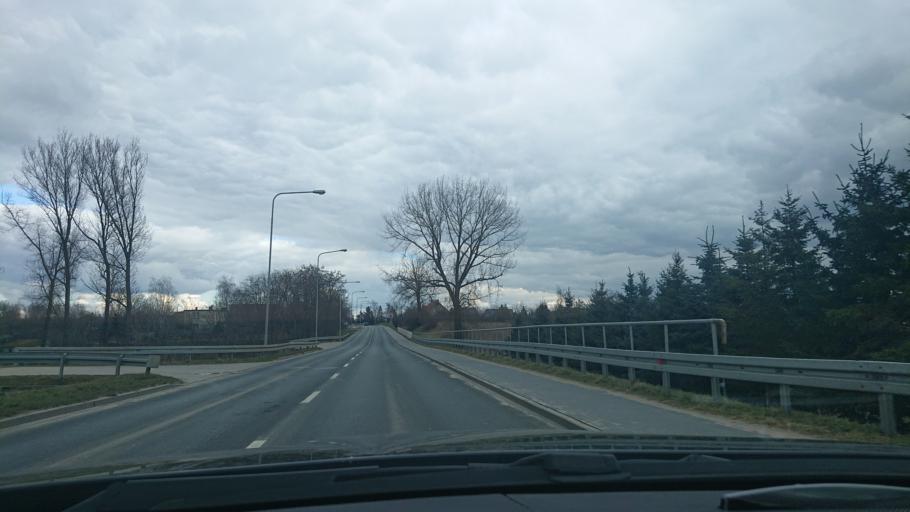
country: PL
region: Greater Poland Voivodeship
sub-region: Powiat gnieznienski
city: Gniezno
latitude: 52.5412
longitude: 17.6367
